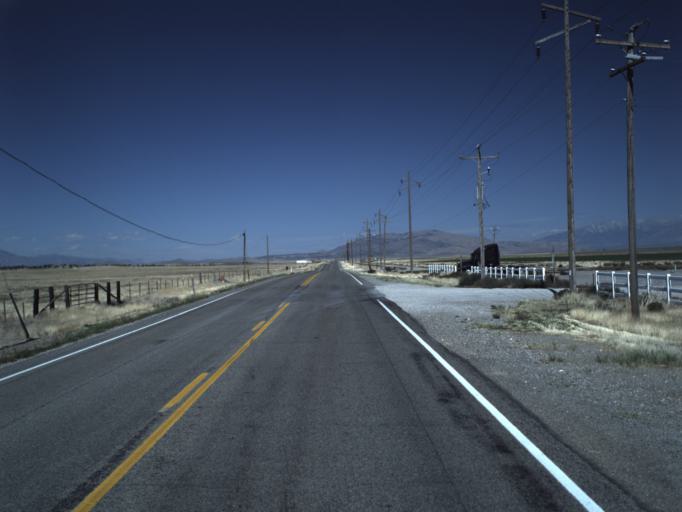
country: US
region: Utah
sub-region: Utah County
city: Genola
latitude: 39.9733
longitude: -111.9569
